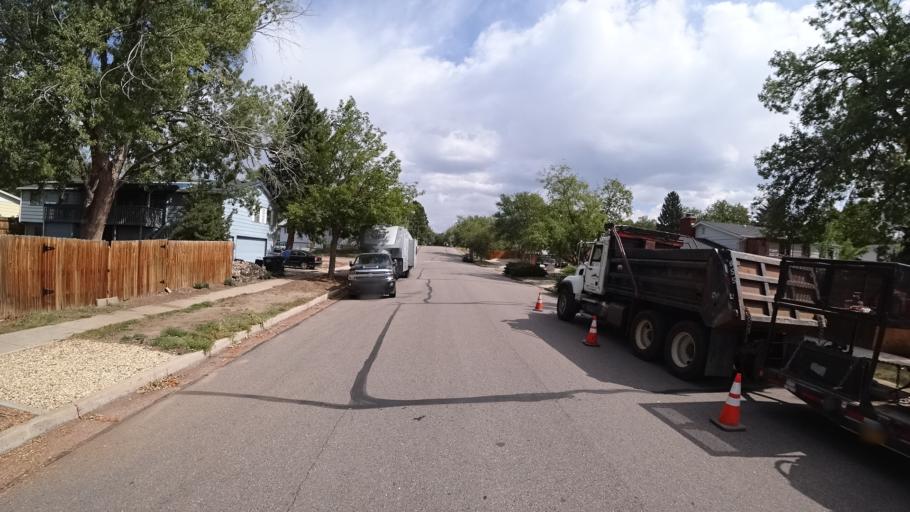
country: US
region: Colorado
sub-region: El Paso County
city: Cimarron Hills
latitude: 38.8517
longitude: -104.7436
